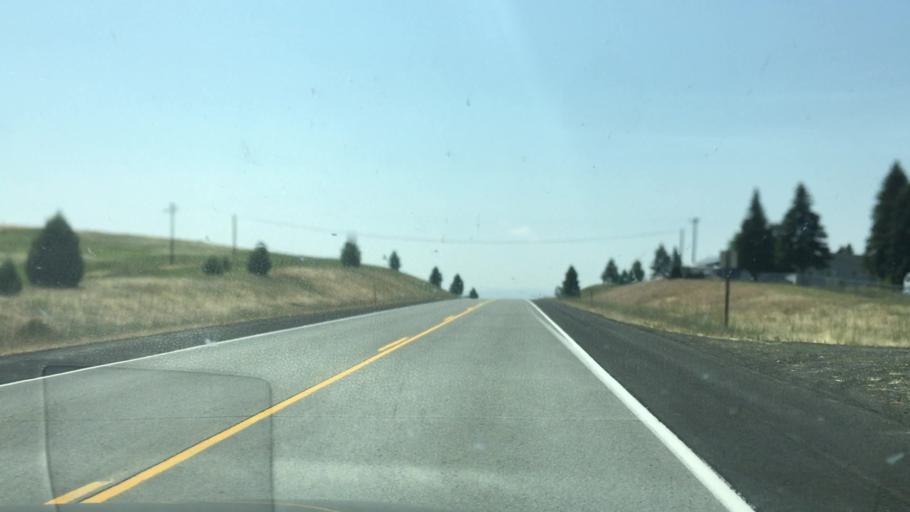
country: US
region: Idaho
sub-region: Lewis County
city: Nezperce
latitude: 46.0572
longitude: -116.3438
